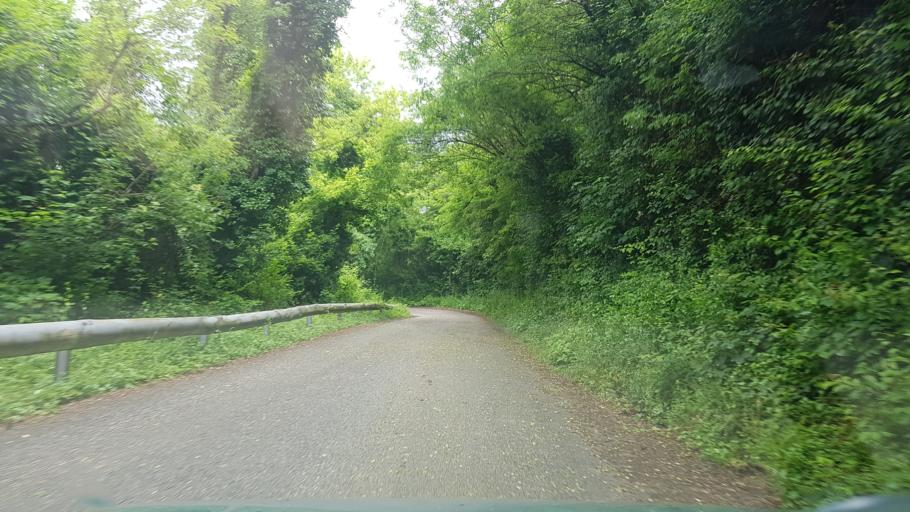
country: IT
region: Friuli Venezia Giulia
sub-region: Provincia di Gorizia
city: San Floriano del Collio
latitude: 45.9504
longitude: 13.5878
